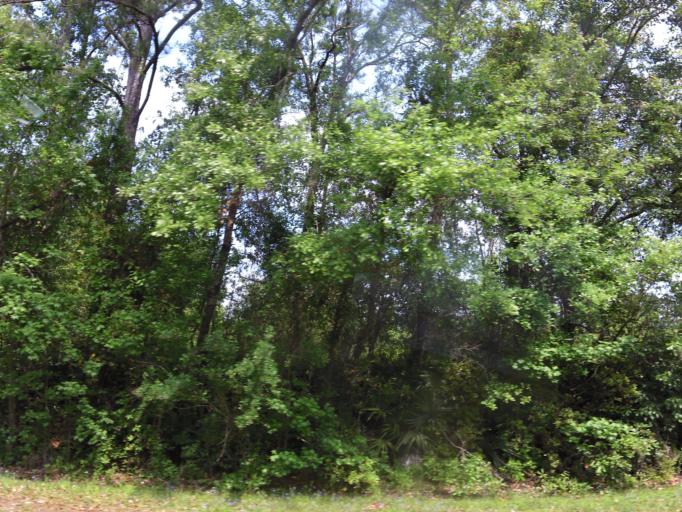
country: US
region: Georgia
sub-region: Camden County
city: Kingsland
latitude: 30.7610
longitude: -81.6584
